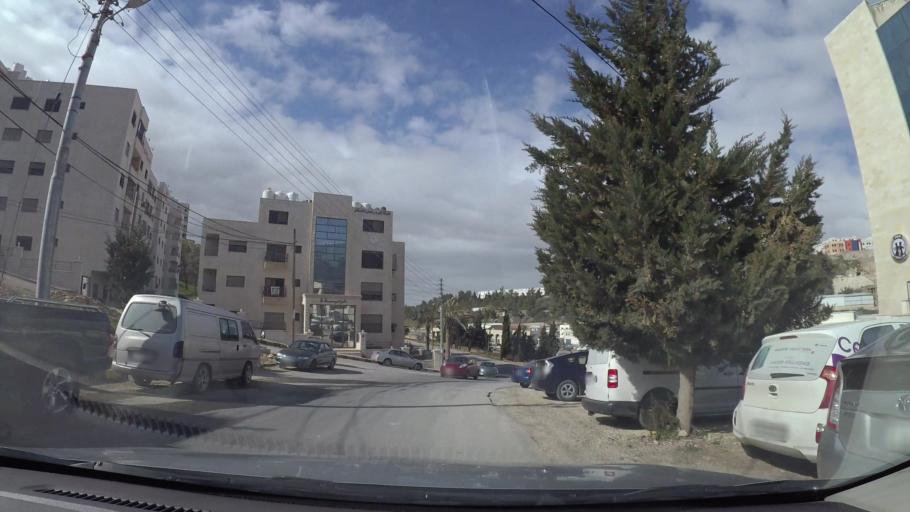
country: JO
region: Amman
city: Al Jubayhah
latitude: 32.0117
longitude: 35.8425
